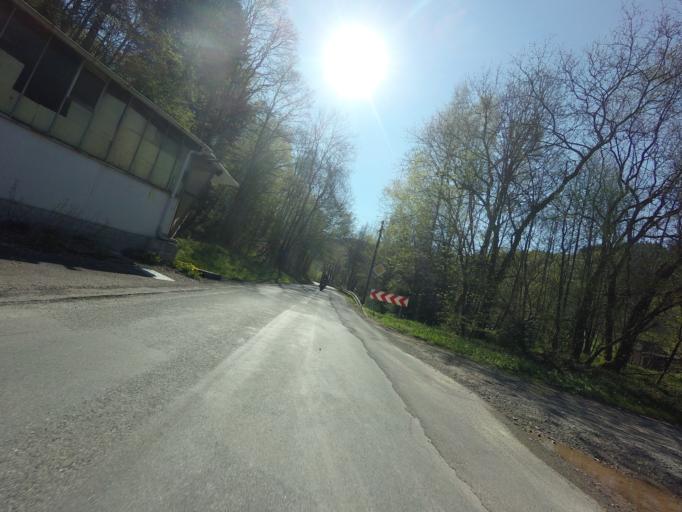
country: DE
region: North Rhine-Westphalia
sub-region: Regierungsbezirk Arnsberg
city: Herscheid
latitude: 51.1036
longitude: 7.7271
